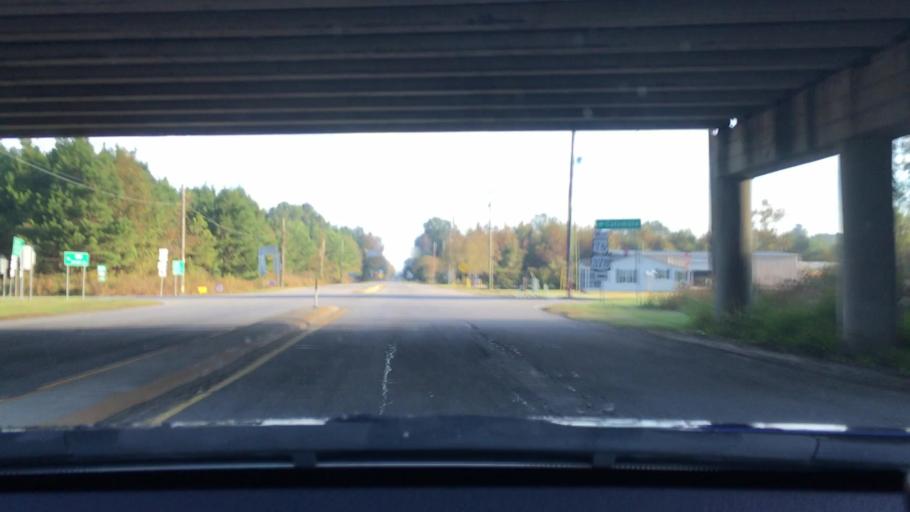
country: US
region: South Carolina
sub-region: Sumter County
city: East Sumter
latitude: 33.9371
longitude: -80.3196
